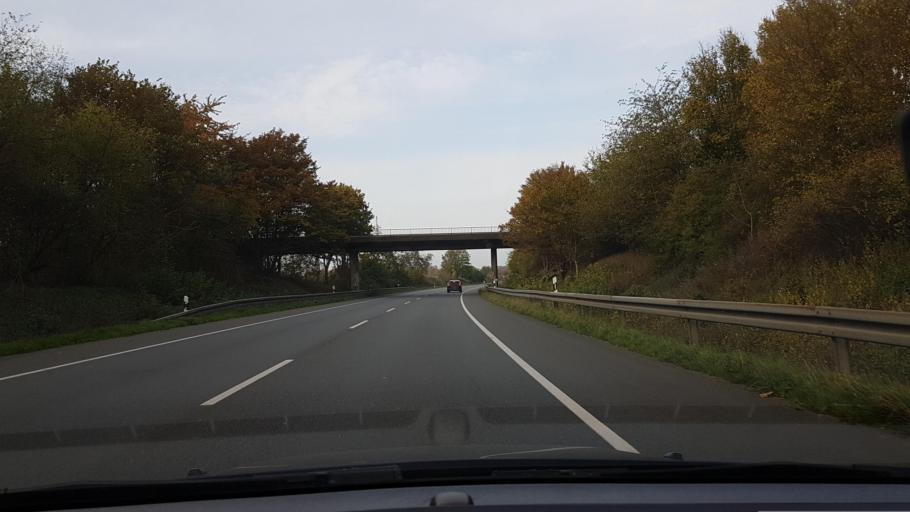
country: DE
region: Lower Saxony
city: Wunstorf
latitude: 52.4234
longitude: 9.4636
